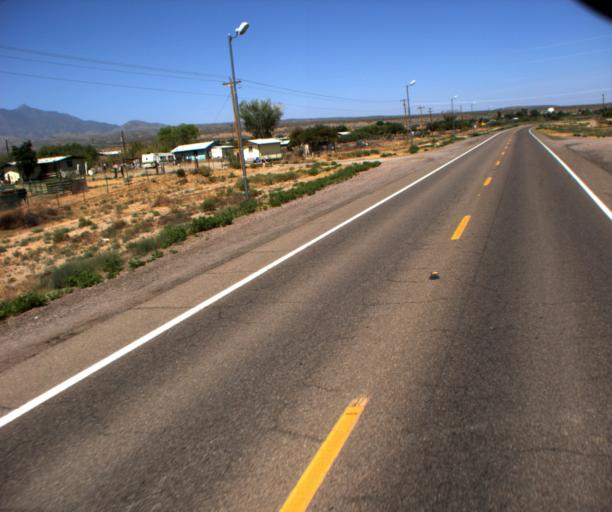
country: US
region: Arizona
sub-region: Graham County
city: Bylas
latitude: 33.1145
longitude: -110.1022
